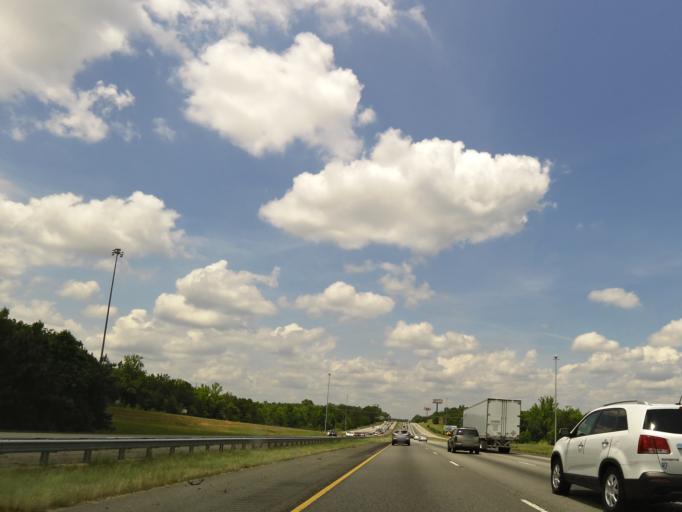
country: US
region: Georgia
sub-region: Henry County
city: Locust Grove
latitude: 33.2623
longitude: -84.0958
